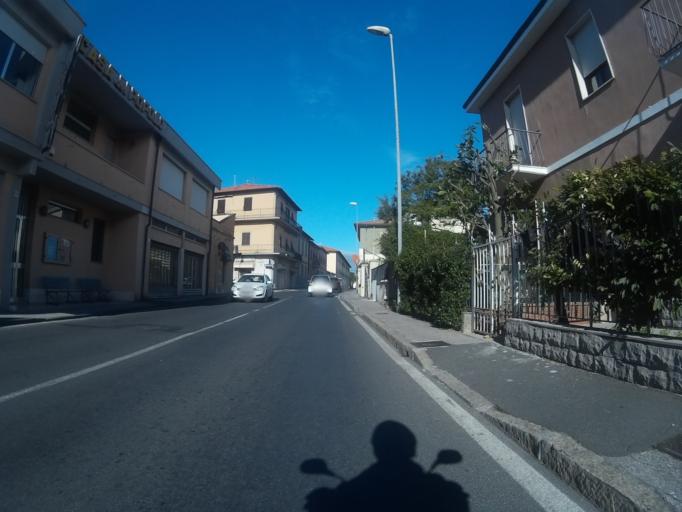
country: IT
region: Tuscany
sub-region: Provincia di Livorno
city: Livorno
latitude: 43.5354
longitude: 10.3420
